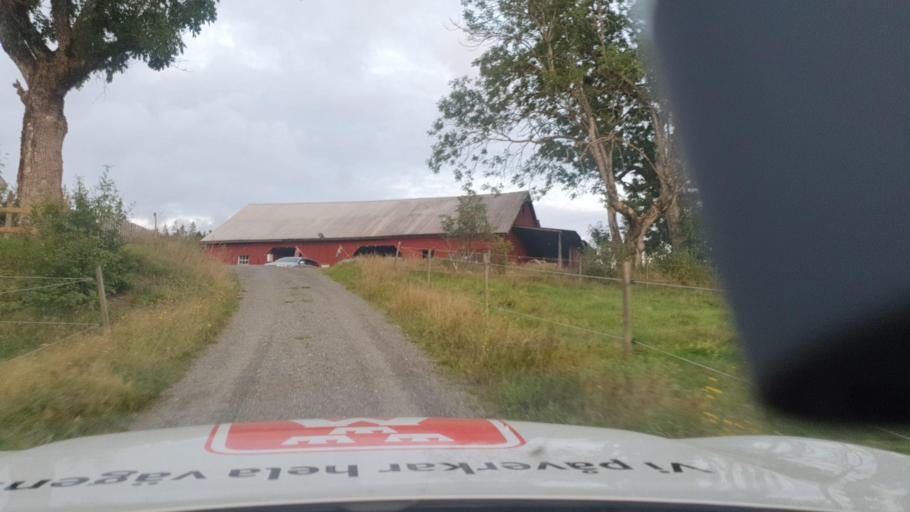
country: SE
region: Vaestra Goetaland
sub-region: Harryda Kommun
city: Hindas
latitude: 57.6876
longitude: 12.4740
